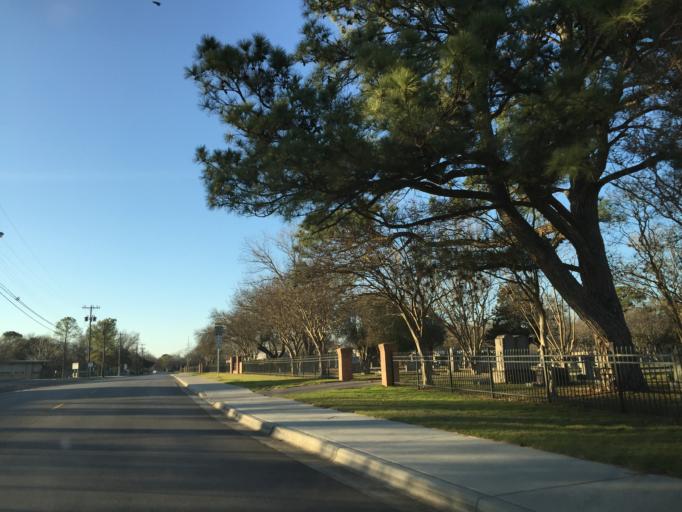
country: US
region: Texas
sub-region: Bastrop County
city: Elgin
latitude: 30.3478
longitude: -97.3779
